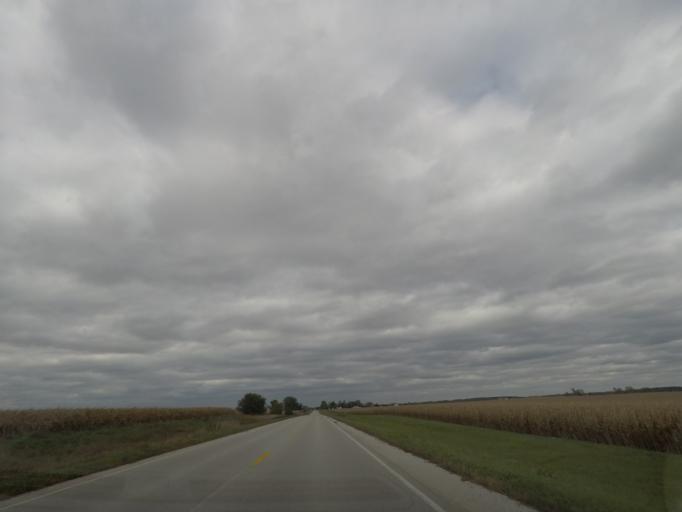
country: US
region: Iowa
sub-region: Story County
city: Huxley
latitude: 41.8715
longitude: -93.5315
